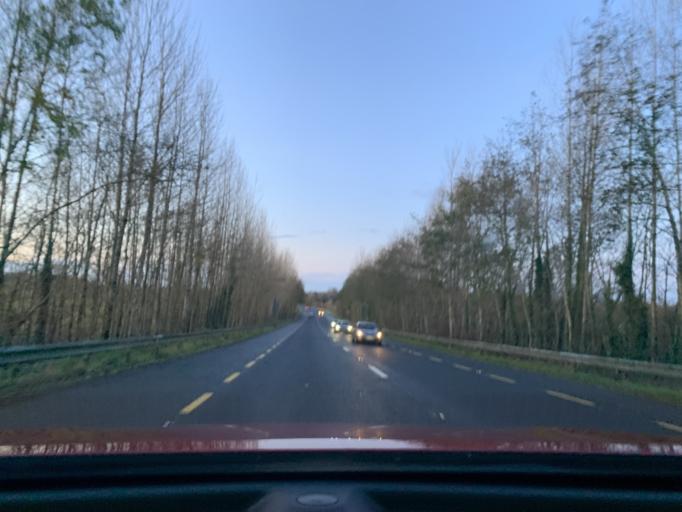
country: IE
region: Connaught
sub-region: County Leitrim
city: Carrick-on-Shannon
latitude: 53.9043
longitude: -7.9593
